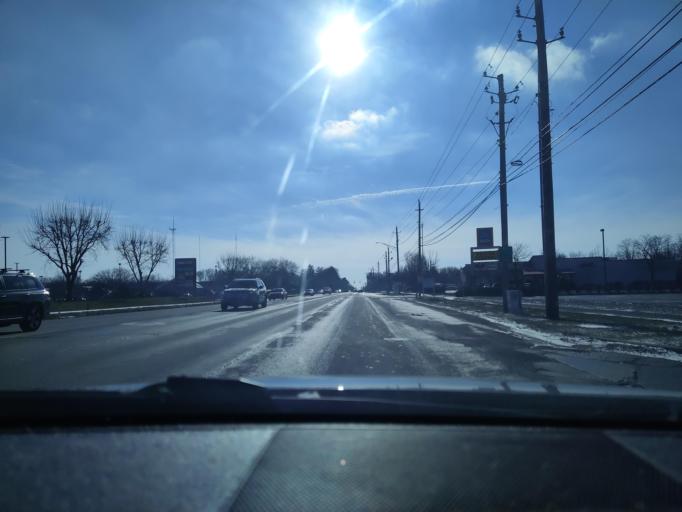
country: US
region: Indiana
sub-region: Boone County
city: Zionsville
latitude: 39.9078
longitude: -86.2209
